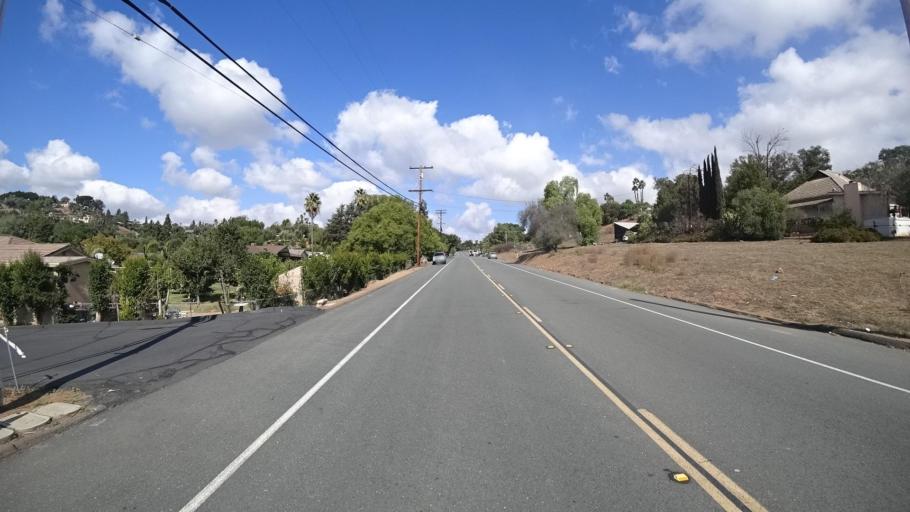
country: US
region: California
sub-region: San Diego County
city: Rancho San Diego
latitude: 32.7635
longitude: -116.9418
